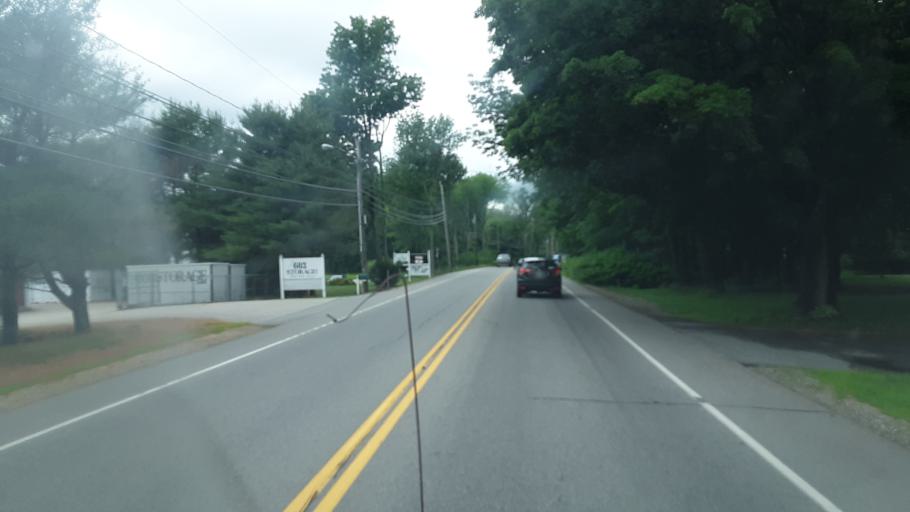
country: US
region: New Hampshire
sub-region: Rockingham County
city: Northwood
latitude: 43.2111
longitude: -71.1915
